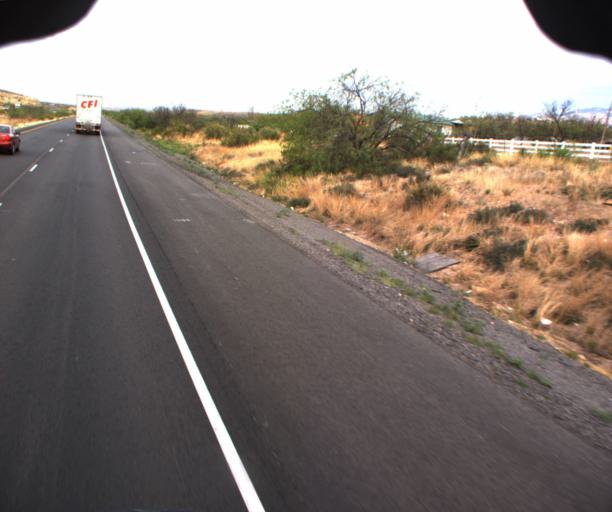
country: US
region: Arizona
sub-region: Cochise County
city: Mescal
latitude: 31.9655
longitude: -110.4598
